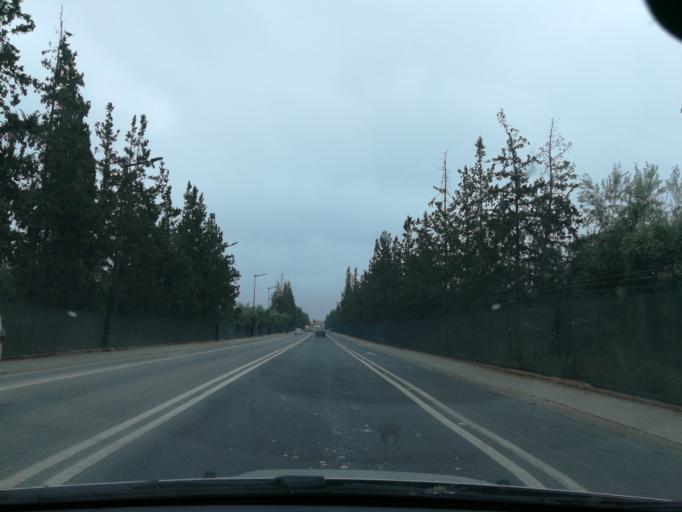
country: MA
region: Marrakech-Tensift-Al Haouz
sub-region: Marrakech
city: Marrakesh
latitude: 31.6025
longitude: -7.9788
